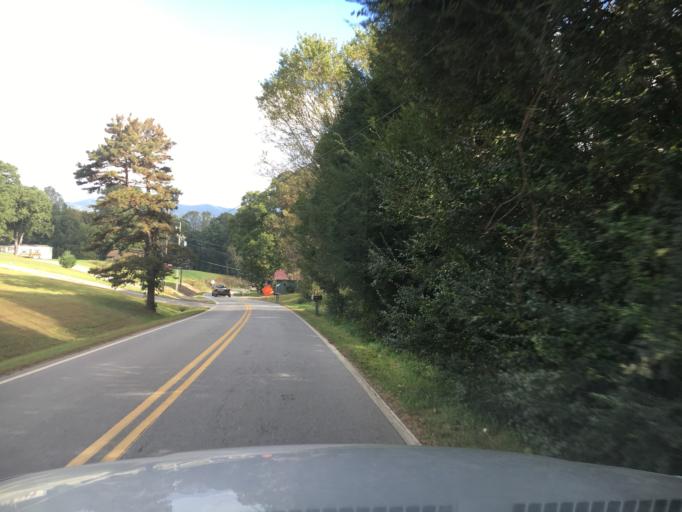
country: US
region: North Carolina
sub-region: Buncombe County
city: Swannanoa
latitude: 35.5962
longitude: -82.4348
